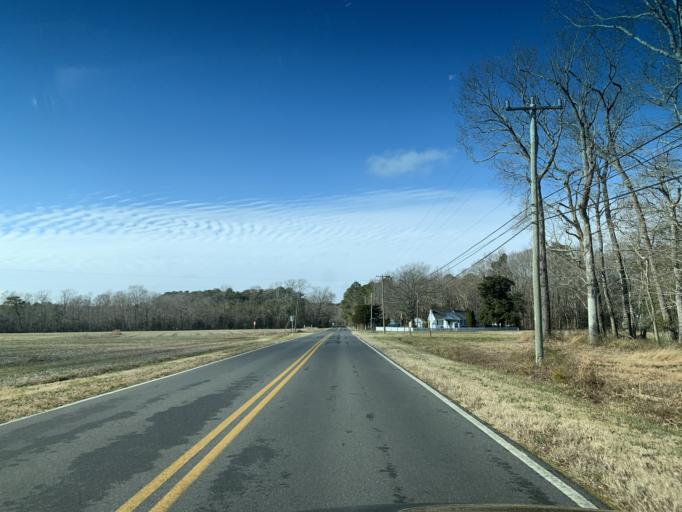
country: US
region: Maryland
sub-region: Worcester County
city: Ocean Pines
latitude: 38.4165
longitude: -75.1244
